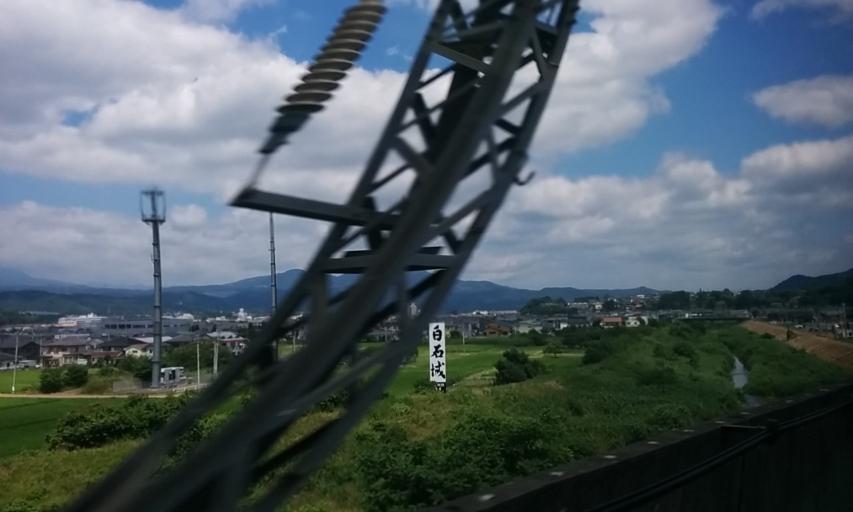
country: JP
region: Miyagi
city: Shiroishi
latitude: 37.9910
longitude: 140.6294
